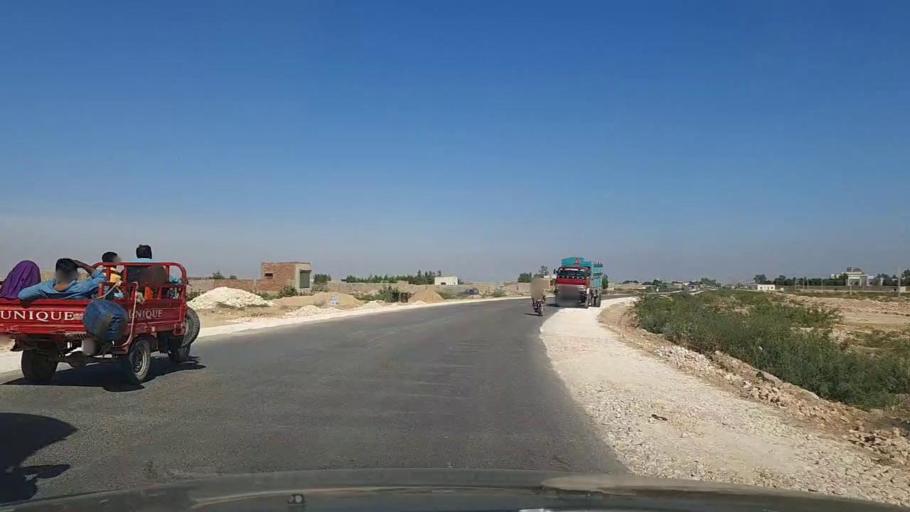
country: PK
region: Sindh
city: Kotri
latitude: 25.3347
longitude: 68.2441
